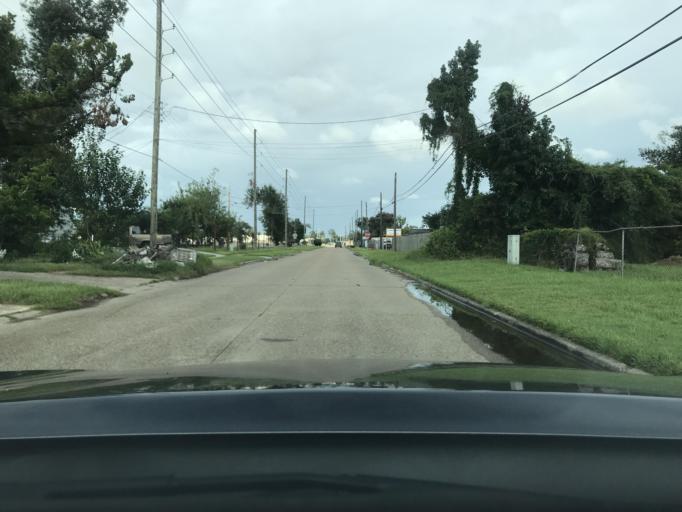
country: US
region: Louisiana
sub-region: Calcasieu Parish
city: Westlake
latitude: 30.2477
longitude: -93.2633
